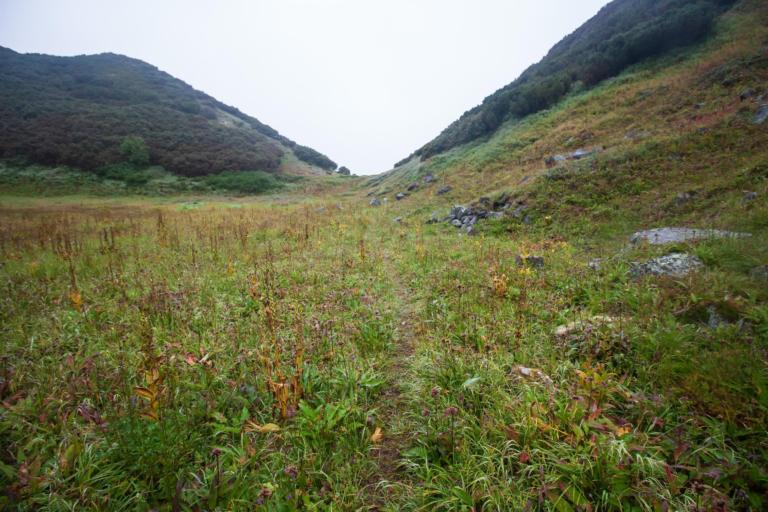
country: RU
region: Kamtsjatka
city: Yelizovo
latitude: 53.9352
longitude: 158.0631
